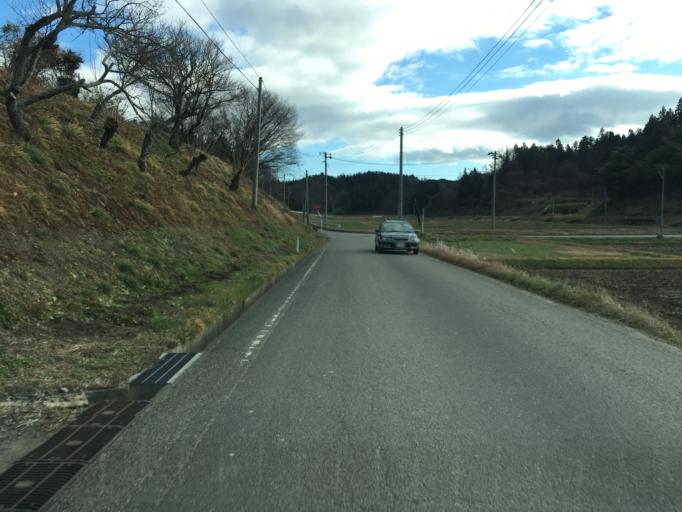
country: JP
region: Fukushima
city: Ishikawa
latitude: 37.2185
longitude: 140.5543
